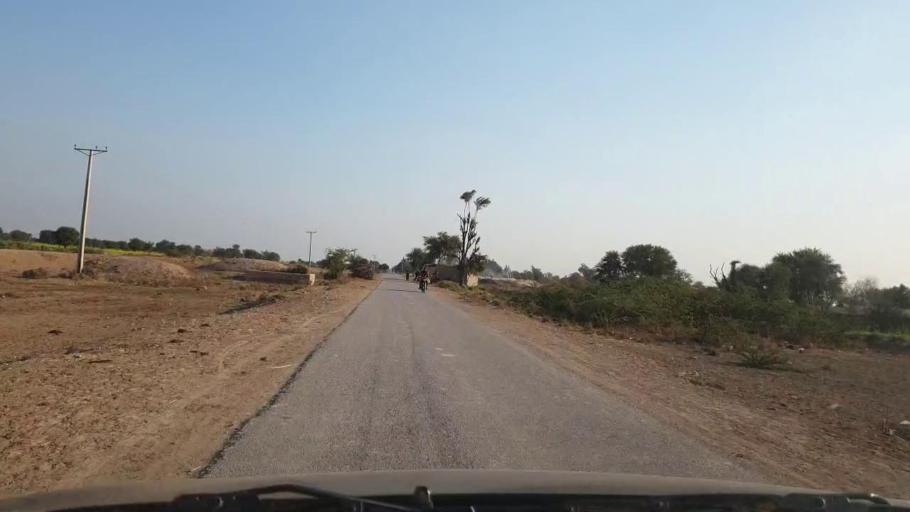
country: PK
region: Sindh
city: Jhol
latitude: 25.9569
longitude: 68.8969
